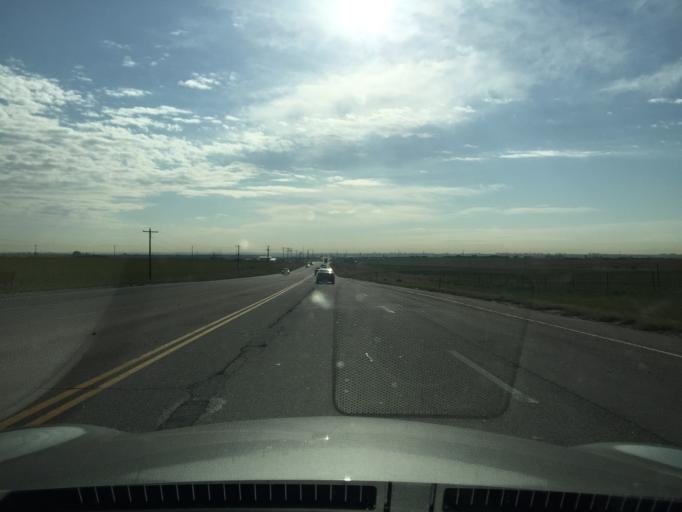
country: US
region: Colorado
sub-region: Boulder County
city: Erie
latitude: 40.0003
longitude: -105.0044
